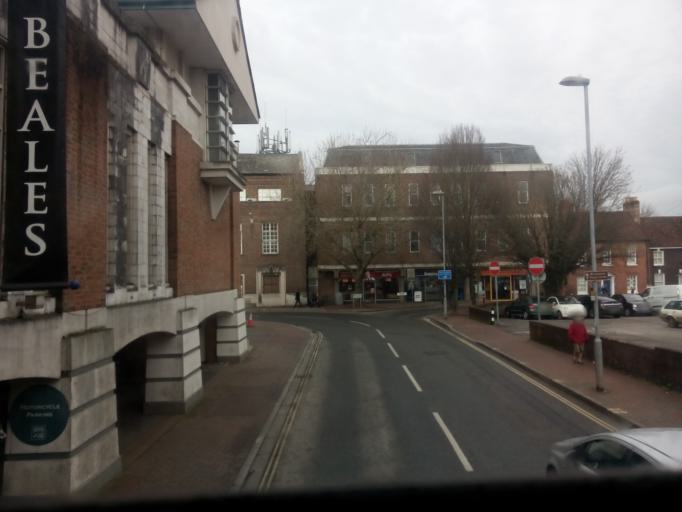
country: GB
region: England
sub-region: Hampshire
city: Winchester
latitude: 51.0634
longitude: -1.3117
